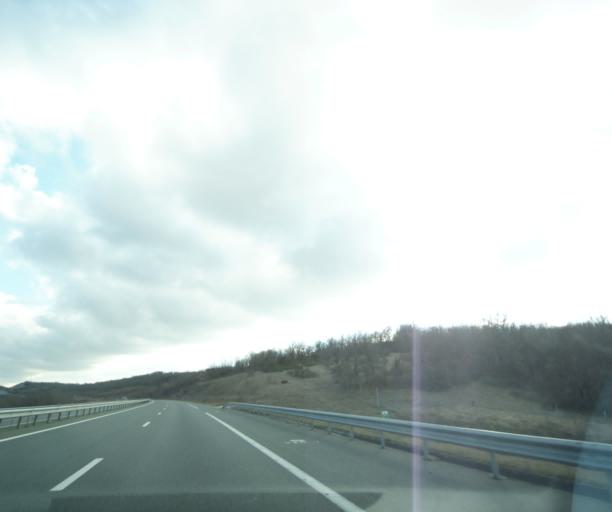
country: FR
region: Midi-Pyrenees
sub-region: Departement du Lot
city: Le Vigan
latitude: 44.7316
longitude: 1.5561
